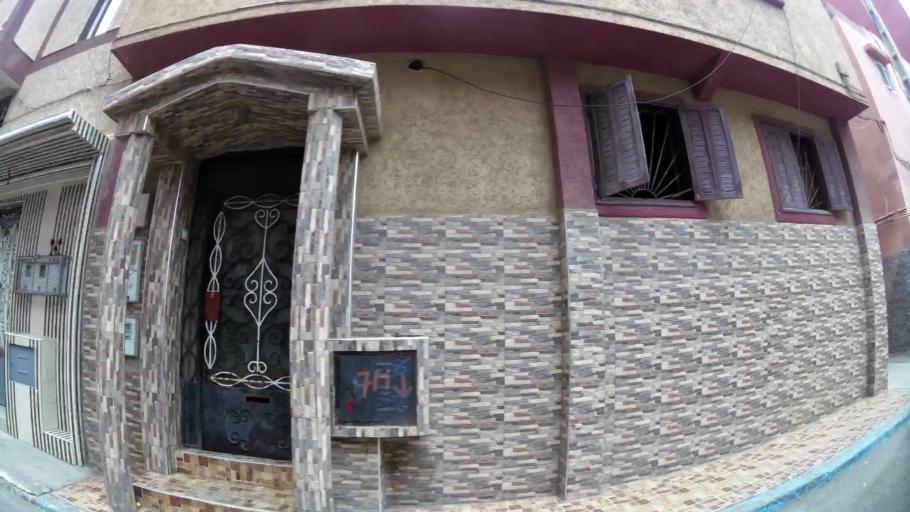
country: MA
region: Rabat-Sale-Zemmour-Zaer
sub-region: Rabat
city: Rabat
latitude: 34.0013
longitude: -6.8650
